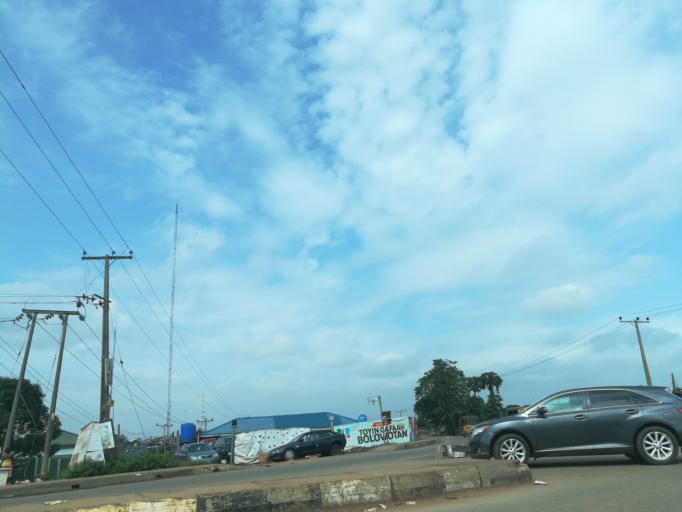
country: NG
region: Lagos
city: Ikorodu
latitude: 6.6326
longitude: 3.5339
